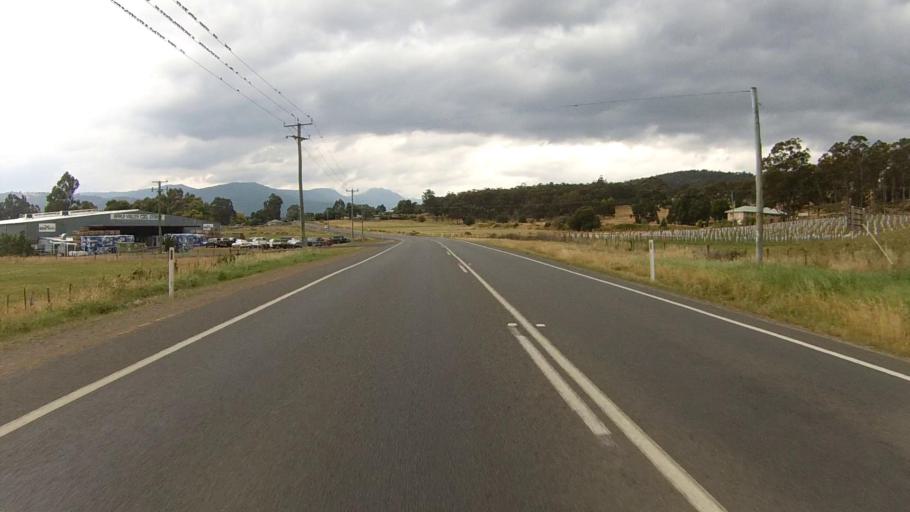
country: AU
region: Tasmania
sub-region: Huon Valley
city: Huonville
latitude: -43.0102
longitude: 147.0654
